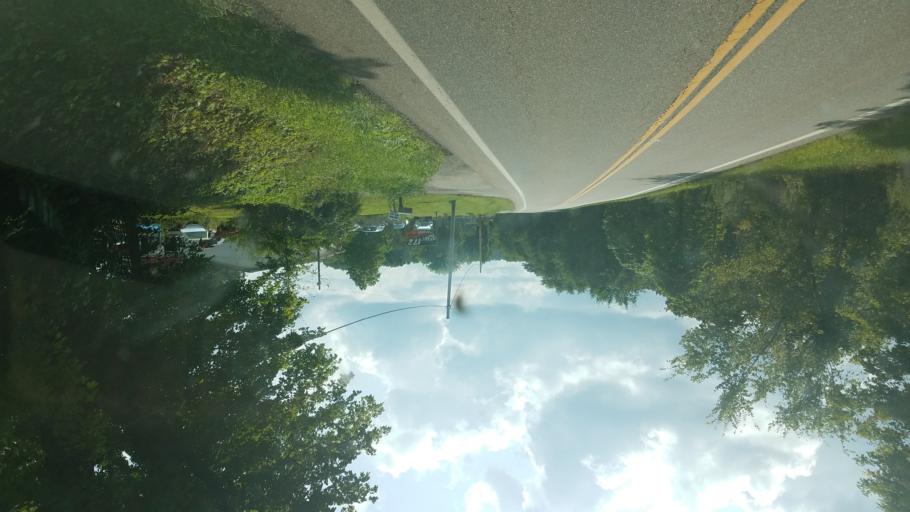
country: US
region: Ohio
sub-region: Columbiana County
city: Lisbon
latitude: 40.7740
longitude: -80.8082
